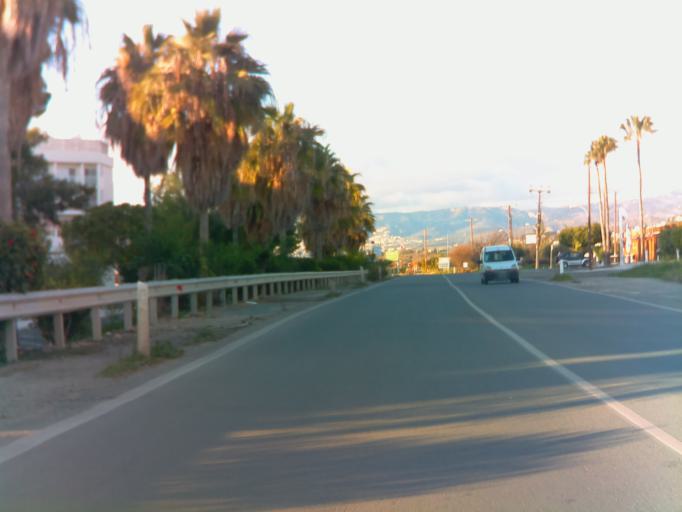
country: CY
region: Pafos
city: Kissonerga
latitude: 34.8061
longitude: 32.3969
